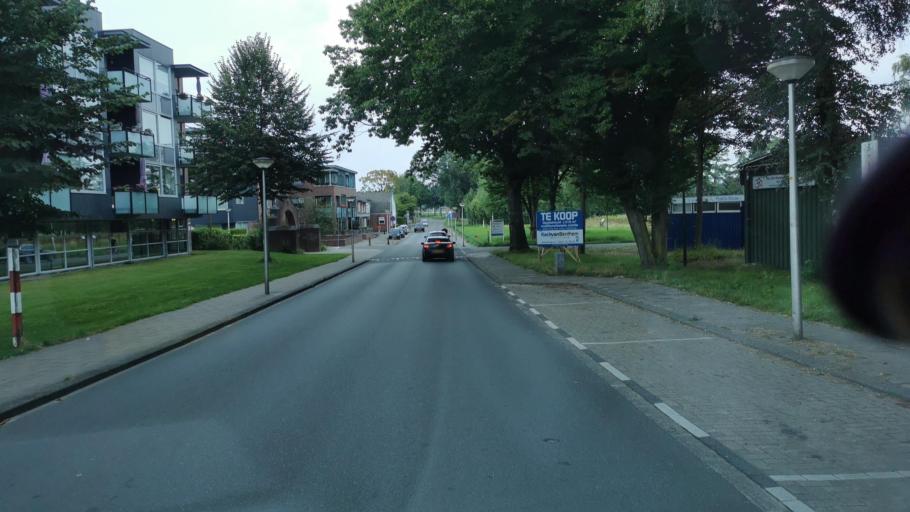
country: DE
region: North Rhine-Westphalia
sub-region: Regierungsbezirk Munster
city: Gronau
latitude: 52.2190
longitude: 6.9735
